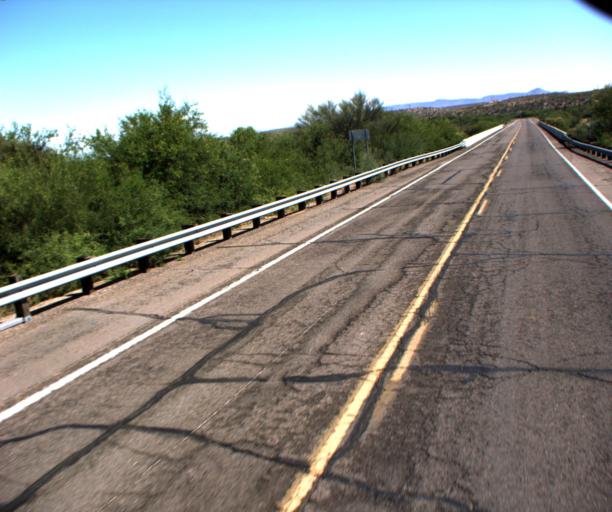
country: US
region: Arizona
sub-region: Pinal County
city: Mammoth
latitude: 32.7415
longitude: -110.6483
